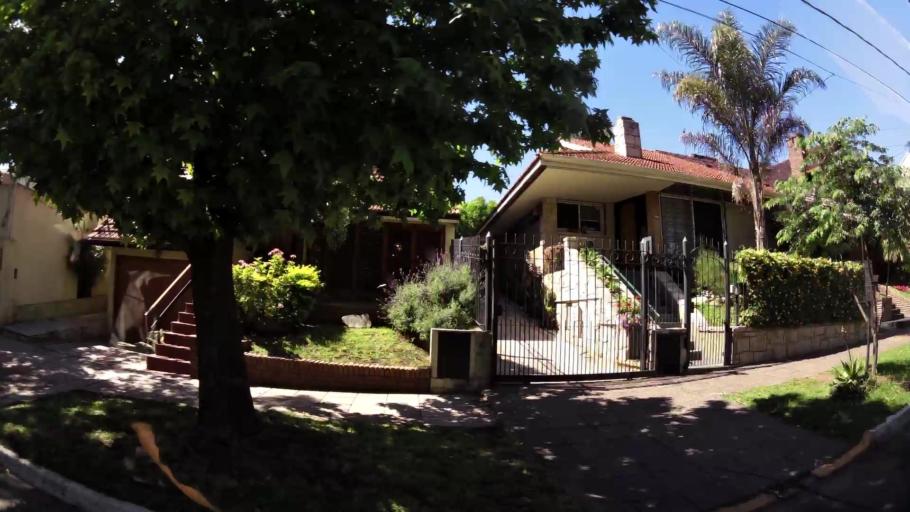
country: AR
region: Buenos Aires
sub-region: Partido de Quilmes
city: Quilmes
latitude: -34.7020
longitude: -58.2878
